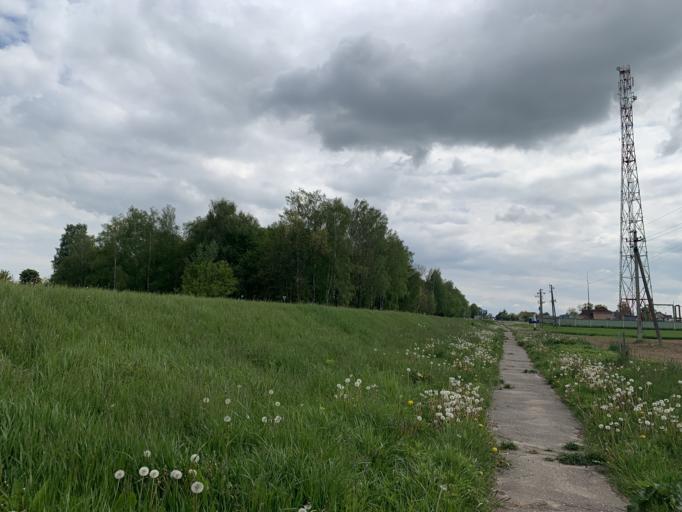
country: BY
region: Minsk
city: Nyasvizh
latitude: 53.2377
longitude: 26.6769
